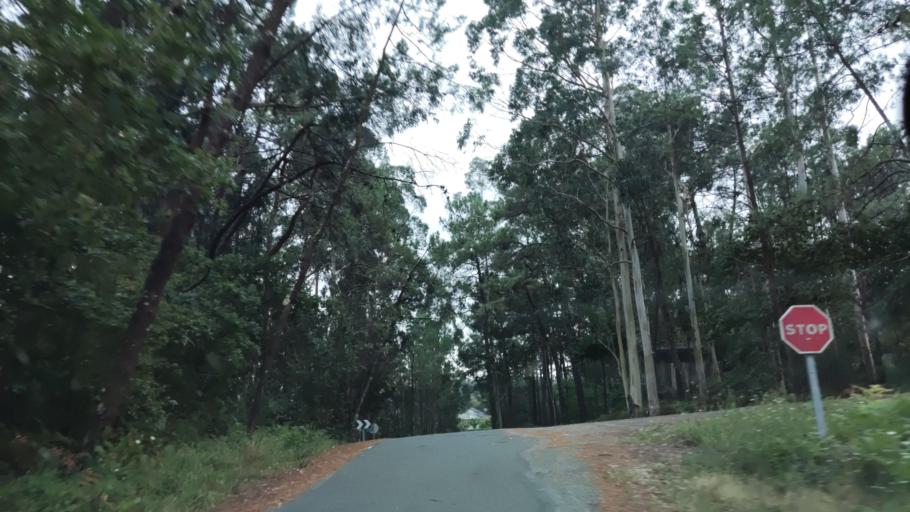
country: ES
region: Galicia
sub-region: Provincia de Pontevedra
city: Catoira
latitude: 42.6911
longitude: -8.7331
